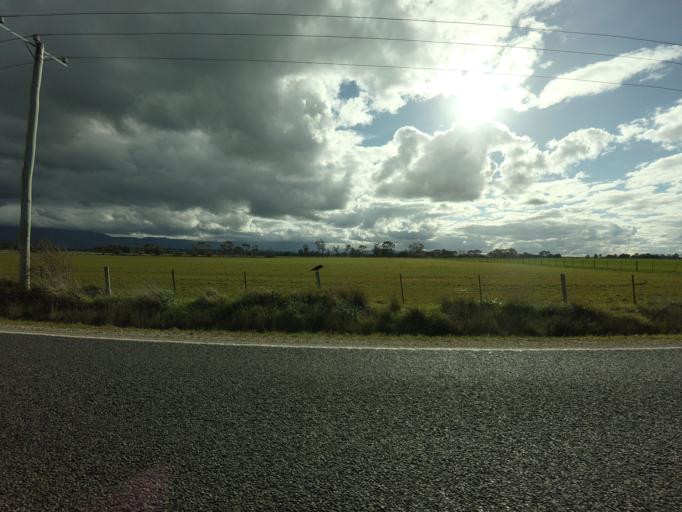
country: AU
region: Tasmania
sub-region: Northern Midlands
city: Longford
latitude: -41.7322
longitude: 147.0860
